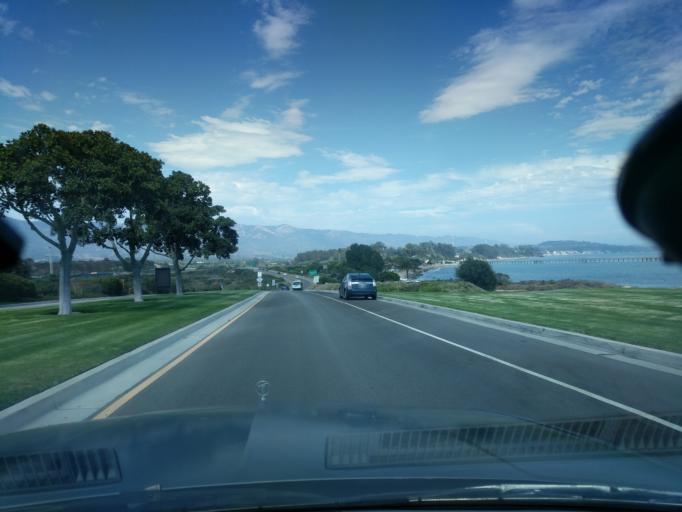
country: US
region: California
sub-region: Santa Barbara County
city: Isla Vista
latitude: 34.4153
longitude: -119.8381
